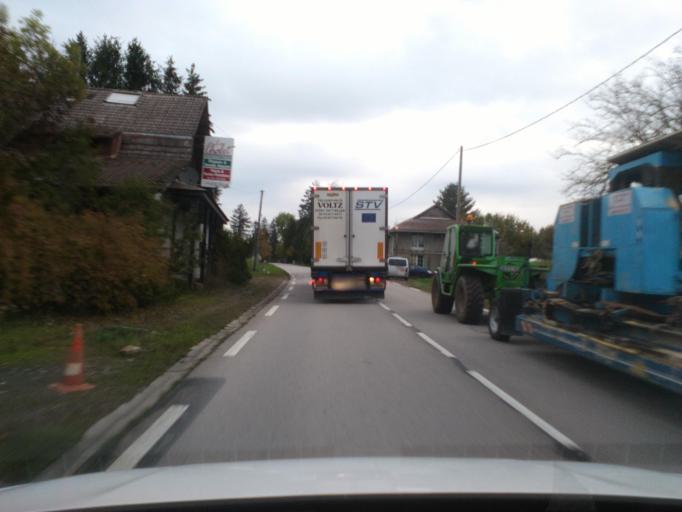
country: FR
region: Lorraine
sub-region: Departement des Vosges
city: Ban-de-Laveline
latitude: 48.3408
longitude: 7.1049
